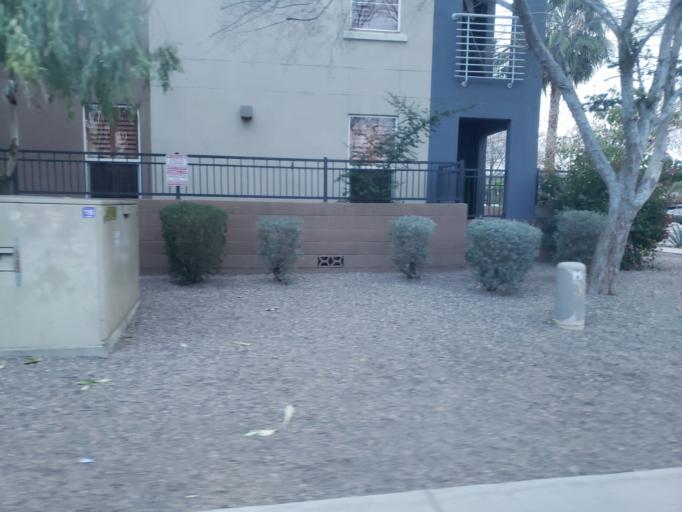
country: US
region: Arizona
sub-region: Maricopa County
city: Phoenix
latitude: 33.4485
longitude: -112.0649
